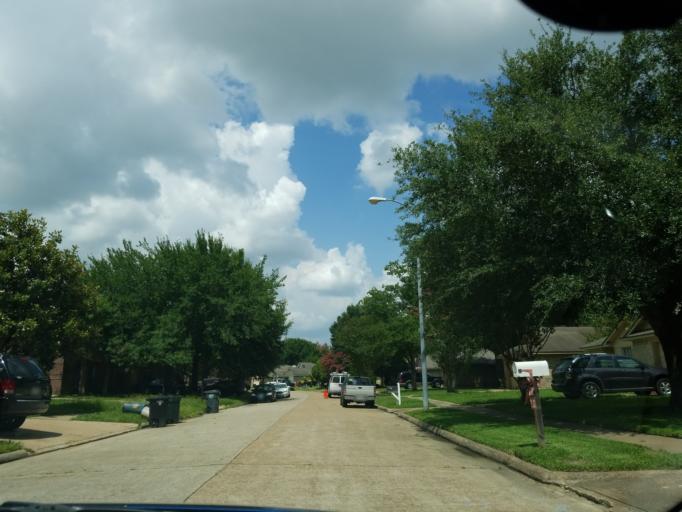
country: US
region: Texas
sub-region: Harris County
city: Cypress
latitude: 29.8720
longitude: -95.7317
